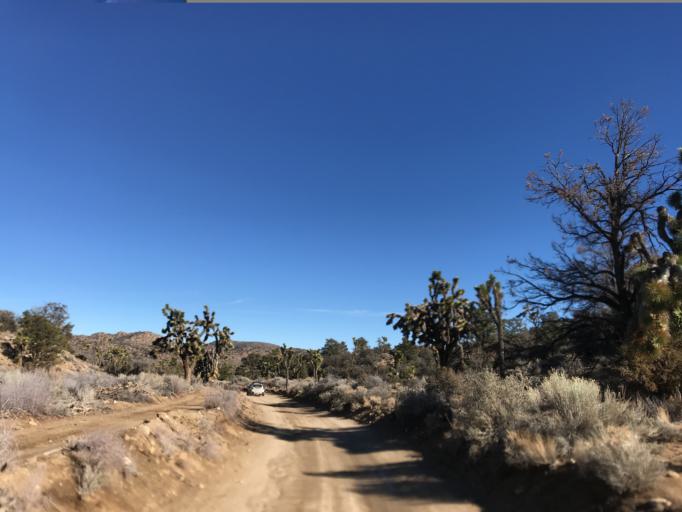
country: US
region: California
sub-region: San Bernardino County
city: Morongo Valley
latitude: 34.2254
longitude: -116.6322
